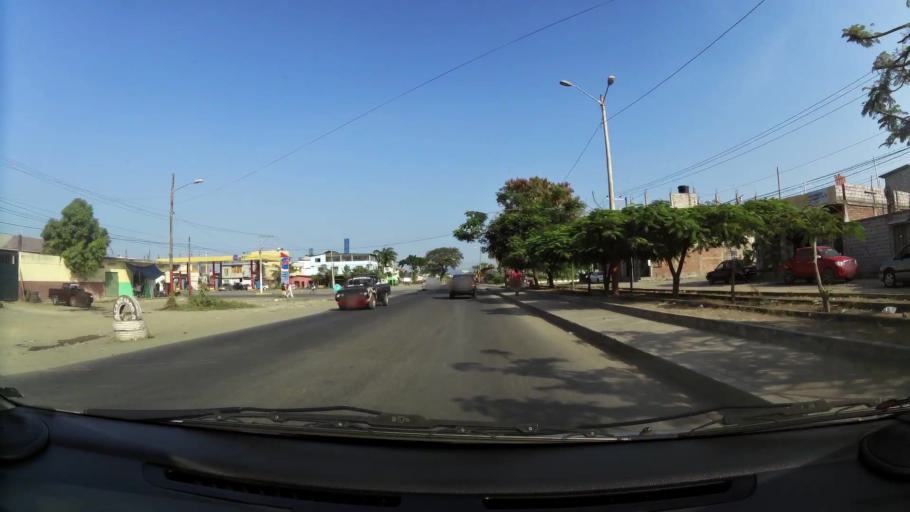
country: EC
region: Guayas
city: Eloy Alfaro
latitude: -2.1813
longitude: -79.8382
